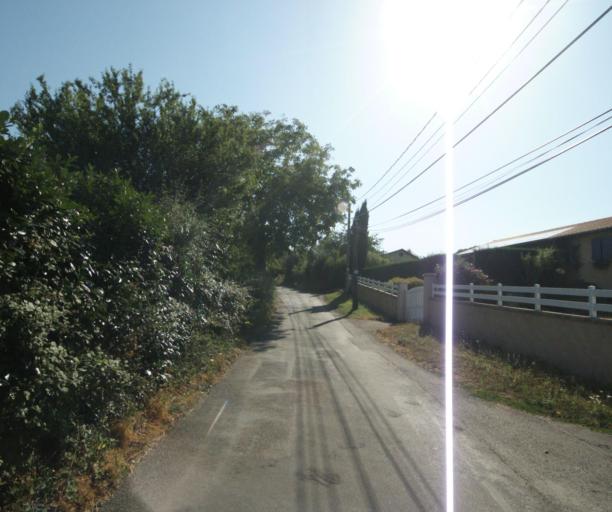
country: FR
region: Rhone-Alpes
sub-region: Departement du Rhone
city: Bessenay
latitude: 45.7788
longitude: 4.5589
